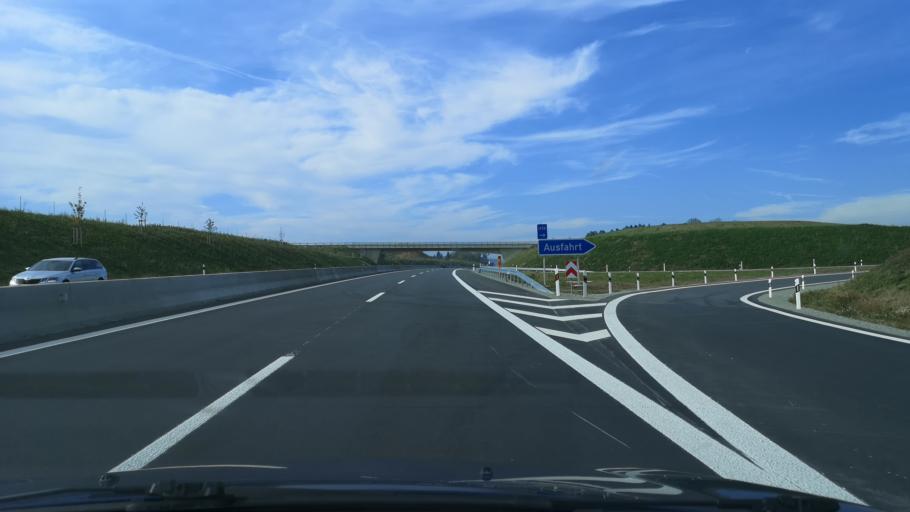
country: DE
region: Bavaria
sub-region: Upper Bavaria
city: Obertaufkirchen
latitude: 48.2499
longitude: 12.2850
